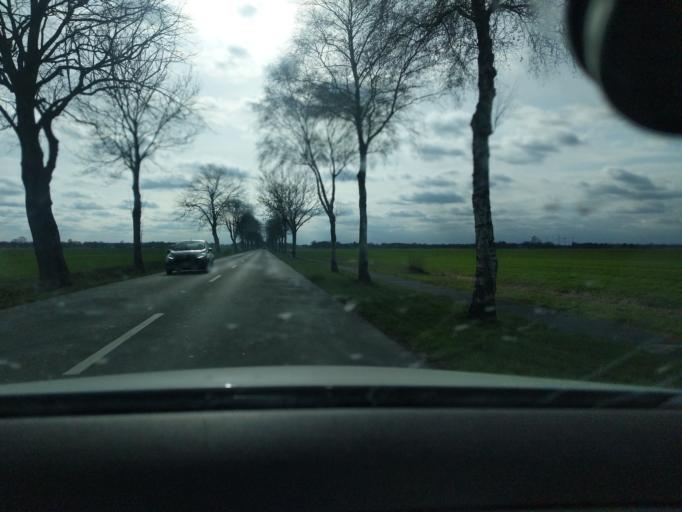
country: DE
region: Lower Saxony
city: Drochtersen
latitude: 53.6817
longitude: 9.3962
